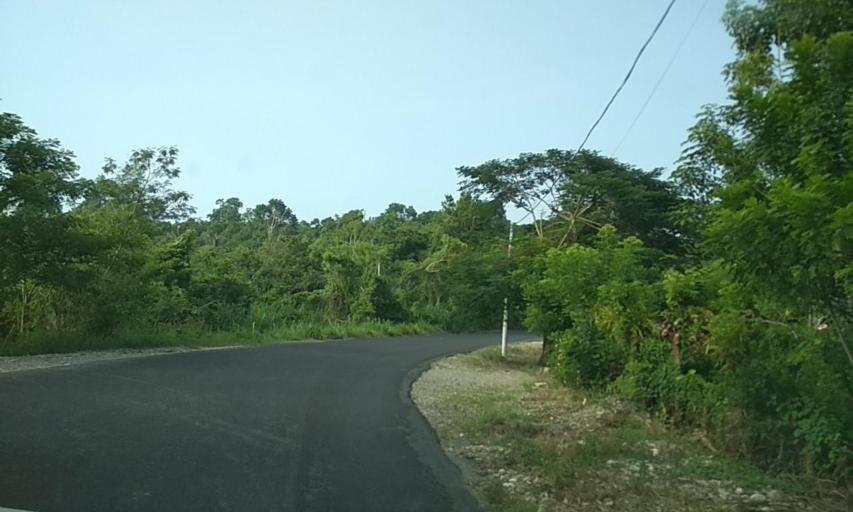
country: MX
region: Veracruz
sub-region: Misantla
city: La Defensa
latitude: 20.0493
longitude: -96.9800
